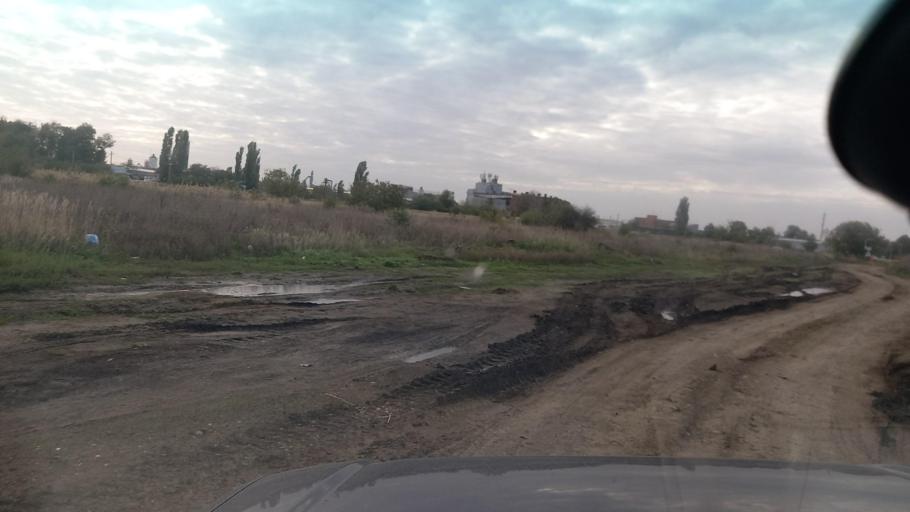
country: RU
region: Krasnodarskiy
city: Krasnodar
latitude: 45.1282
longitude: 38.9117
